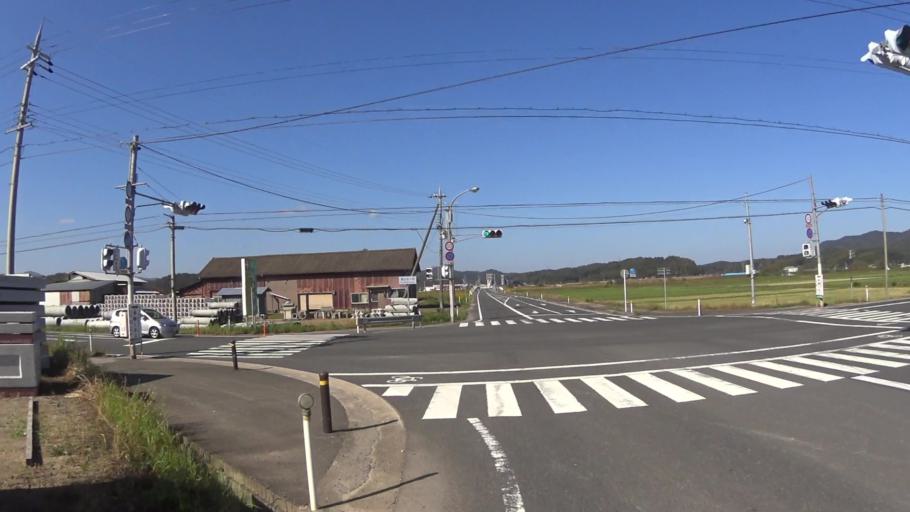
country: JP
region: Kyoto
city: Miyazu
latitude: 35.6694
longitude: 135.0921
